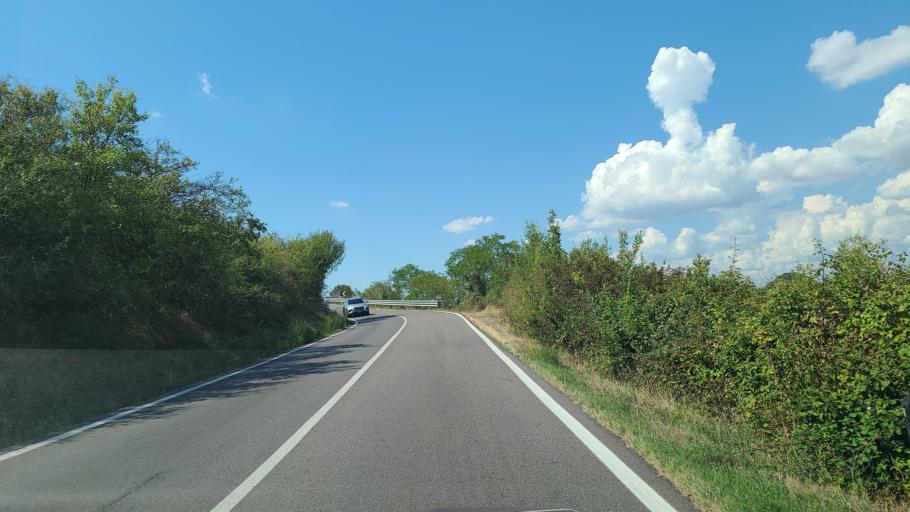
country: IT
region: Tuscany
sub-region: Province of Pisa
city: Volterra
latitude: 43.3871
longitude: 10.9157
